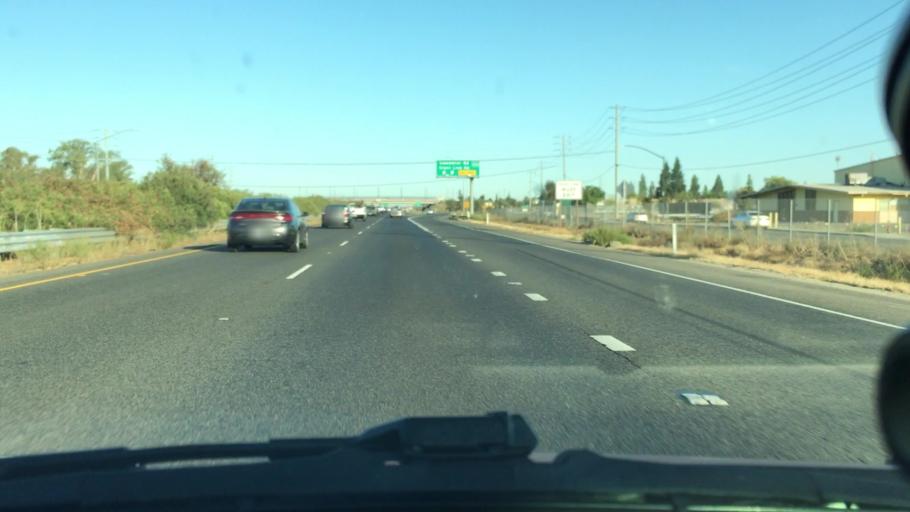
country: US
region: California
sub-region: Sacramento County
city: Elk Grove
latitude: 38.3719
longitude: -121.3574
